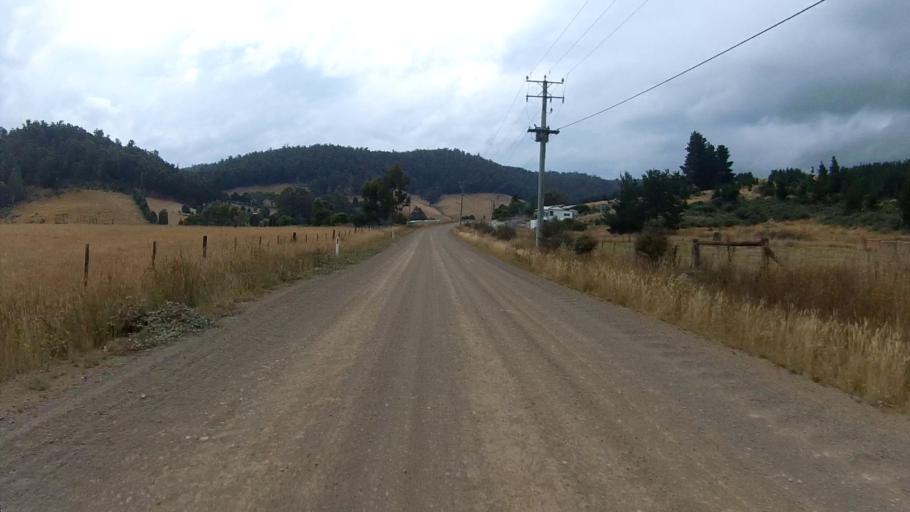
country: AU
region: Tasmania
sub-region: Huon Valley
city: Huonville
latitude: -42.9761
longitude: 147.0547
